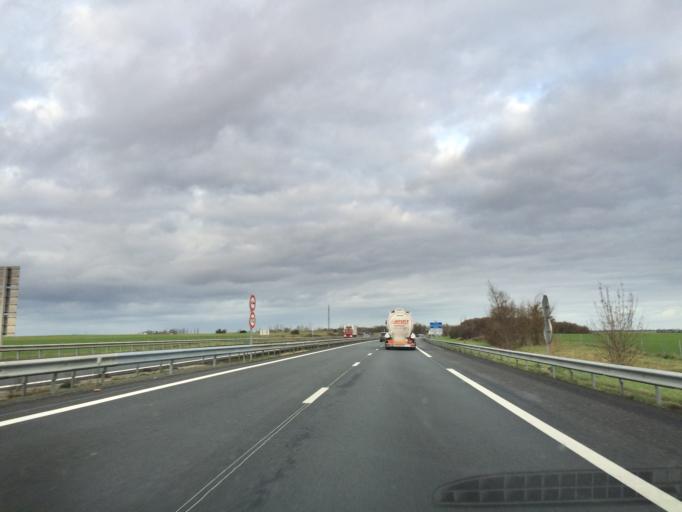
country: FR
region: Poitou-Charentes
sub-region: Departement des Deux-Sevres
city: Aiffres
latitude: 46.2902
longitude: -0.3893
